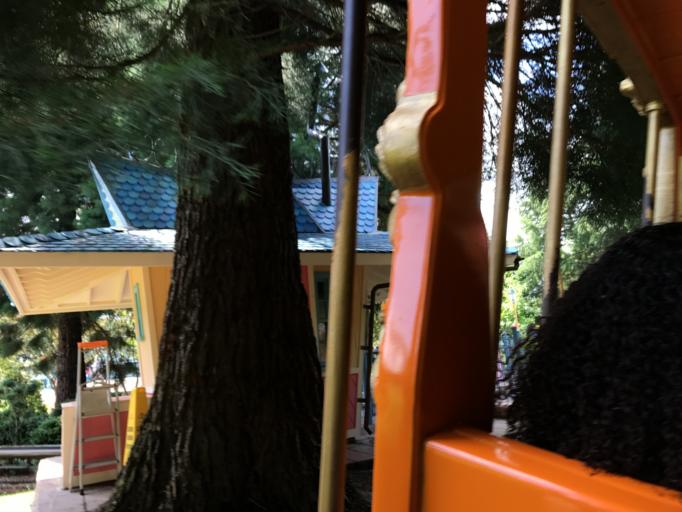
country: FR
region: Ile-de-France
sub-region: Departement de Seine-et-Marne
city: Chessy
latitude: 48.8757
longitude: 2.7744
